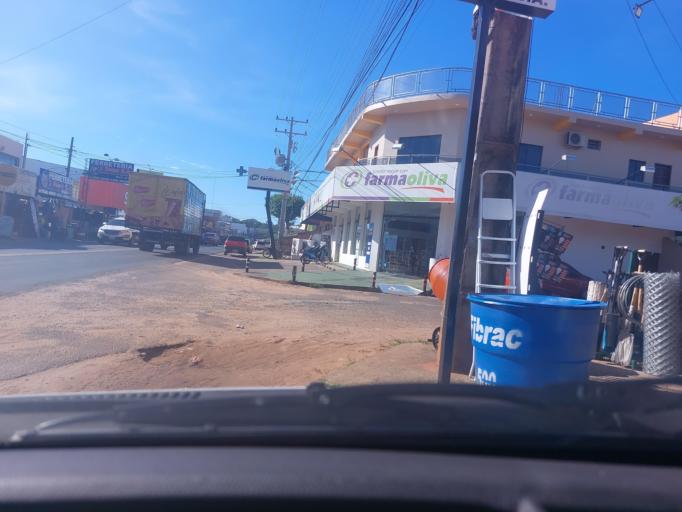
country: PY
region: San Pedro
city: Guayaybi
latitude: -24.6735
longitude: -56.4501
